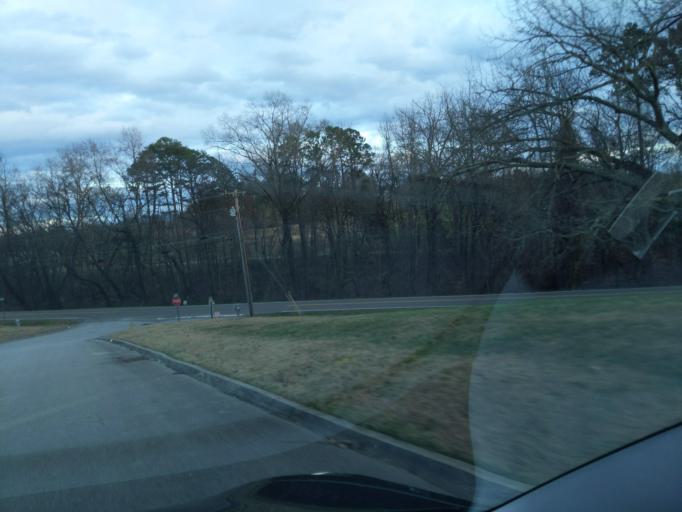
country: US
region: Tennessee
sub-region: Jefferson County
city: Dandridge
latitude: 35.9850
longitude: -83.4641
